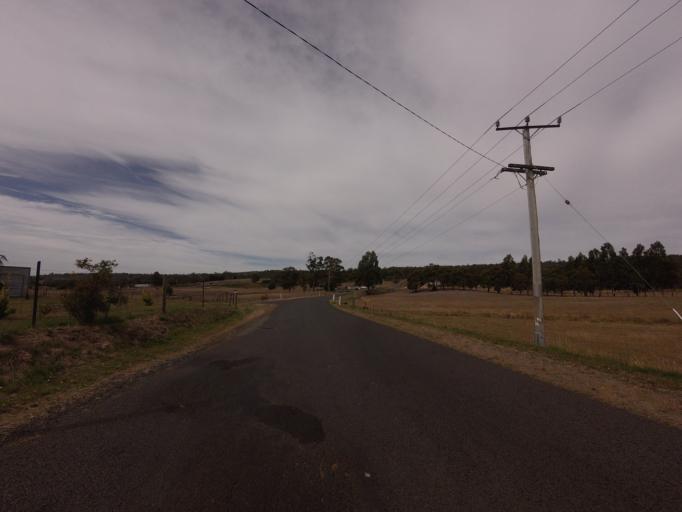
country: AU
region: Tasmania
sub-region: Sorell
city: Sorell
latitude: -42.5623
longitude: 147.5712
